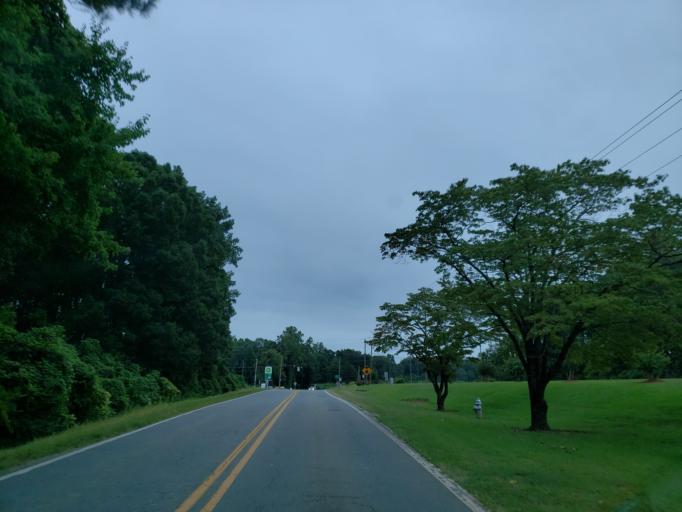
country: US
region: Georgia
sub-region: Cherokee County
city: Canton
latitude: 34.3318
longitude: -84.4882
